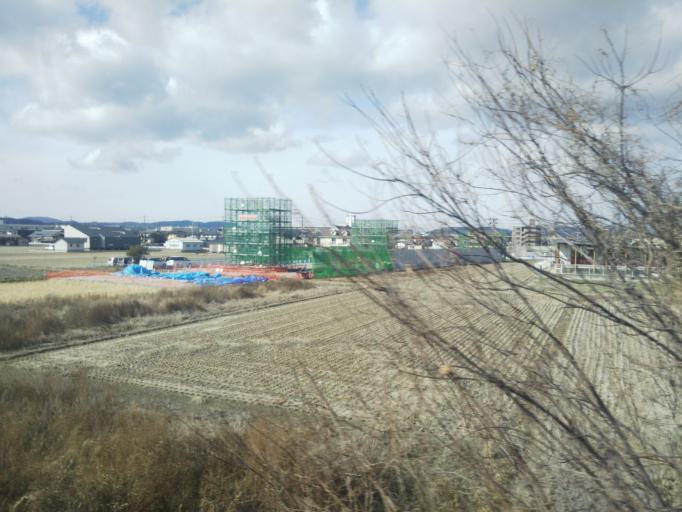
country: JP
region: Okayama
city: Okayama-shi
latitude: 34.6139
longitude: 133.8819
